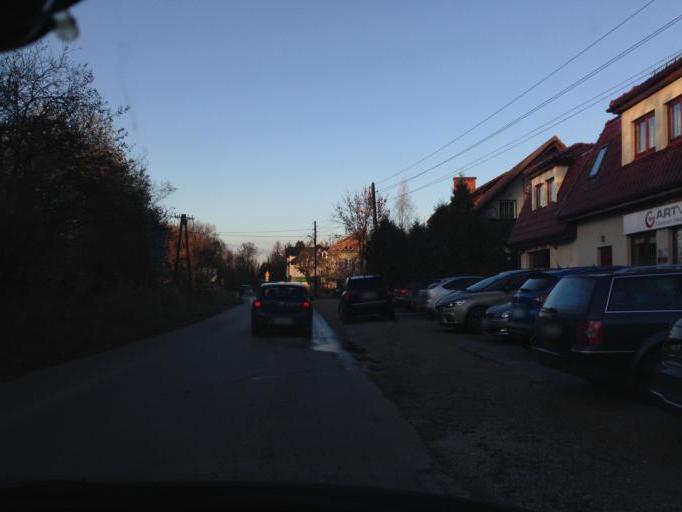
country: PL
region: Lesser Poland Voivodeship
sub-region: Powiat krakowski
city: Rzaska
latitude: 50.0722
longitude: 19.8777
